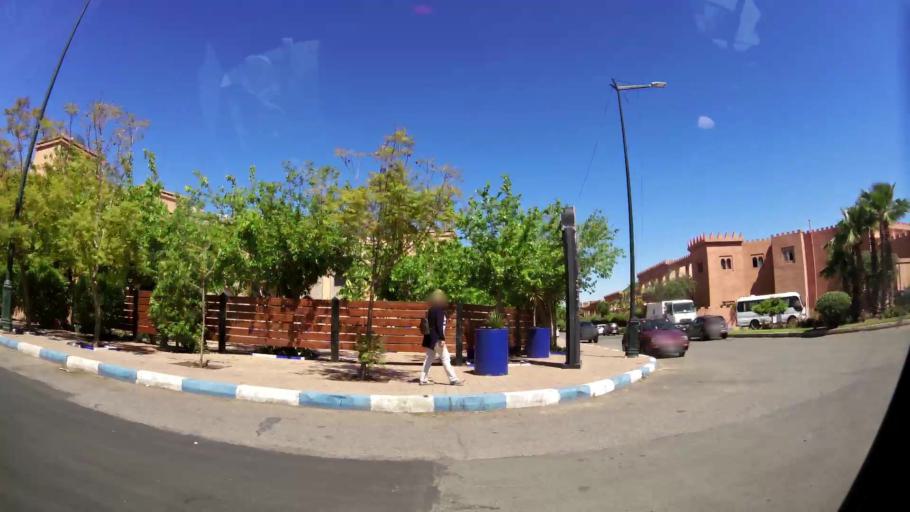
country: MA
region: Marrakech-Tensift-Al Haouz
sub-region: Marrakech
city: Marrakesh
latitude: 31.5964
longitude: -7.9883
